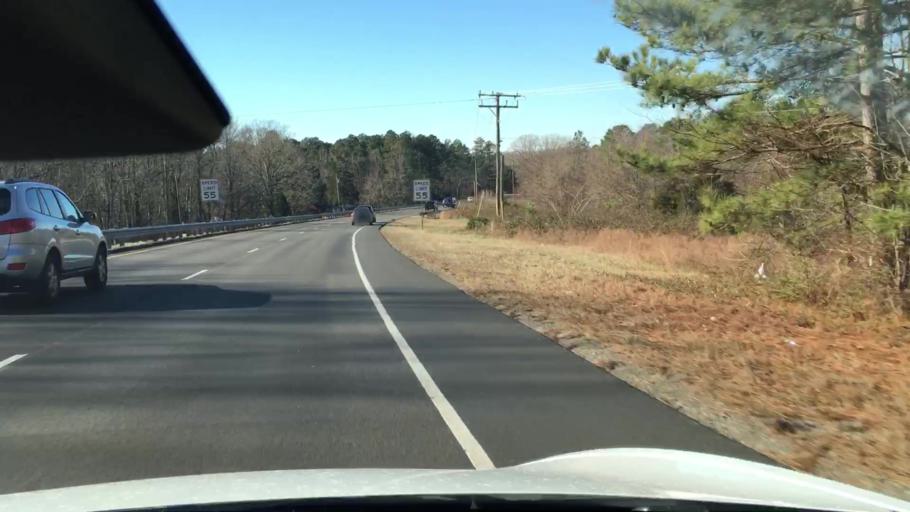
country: US
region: Virginia
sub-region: Chesterfield County
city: Woodlake
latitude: 37.5040
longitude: -77.7181
